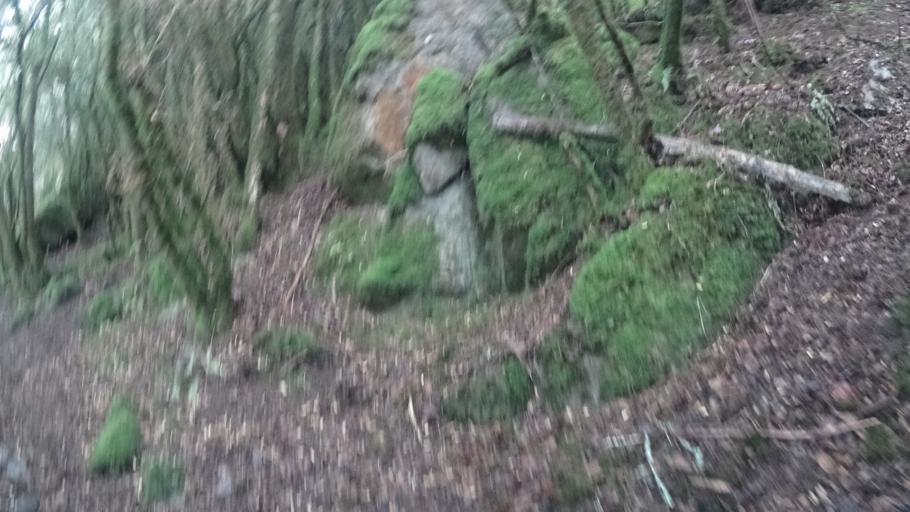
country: FR
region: Aquitaine
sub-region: Departement de la Dordogne
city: Payzac
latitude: 45.3572
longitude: 1.2056
